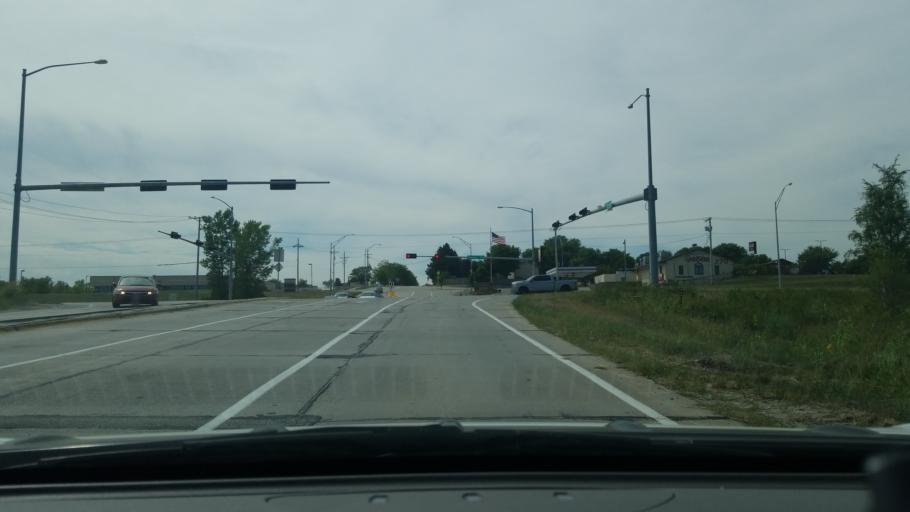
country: US
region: Nebraska
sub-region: Sarpy County
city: Chalco
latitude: 41.1480
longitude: -96.1197
